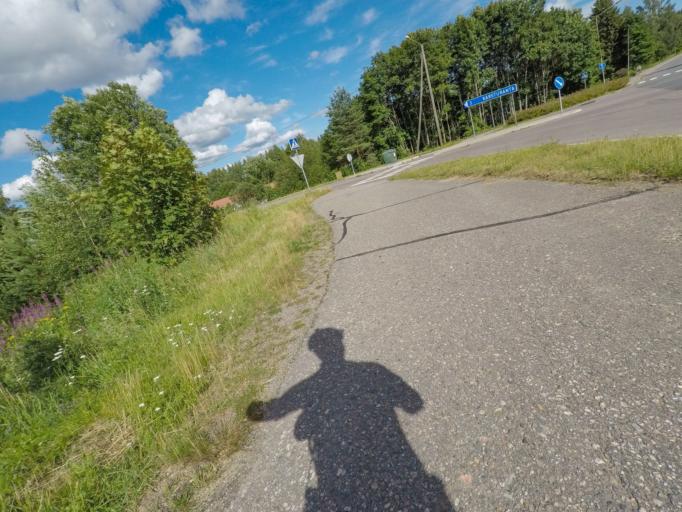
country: FI
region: South Karelia
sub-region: Lappeenranta
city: Joutseno
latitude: 61.1262
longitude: 28.4947
